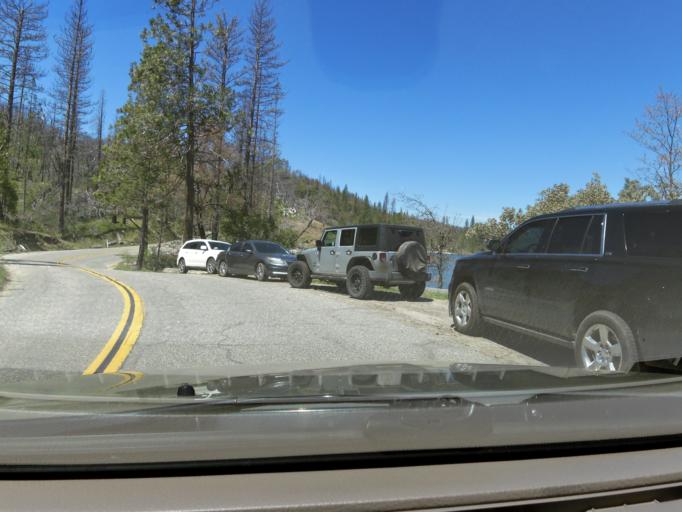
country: US
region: California
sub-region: Madera County
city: Oakhurst
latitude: 37.3172
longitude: -119.5739
